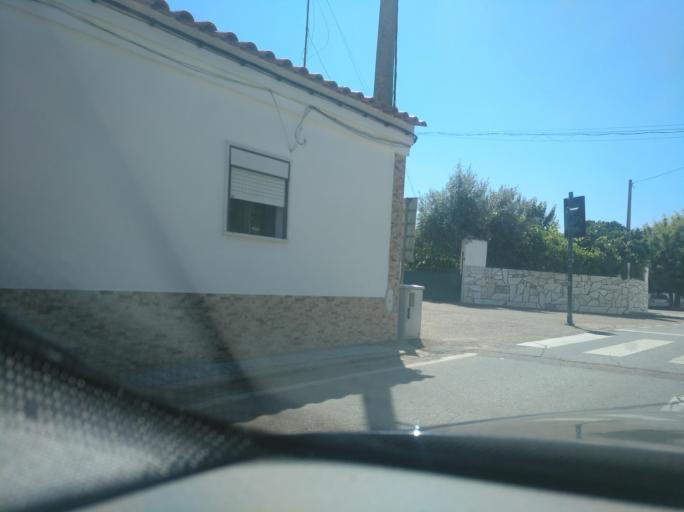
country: PT
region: Portalegre
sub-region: Elvas
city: Elvas
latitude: 38.9610
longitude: -7.2980
